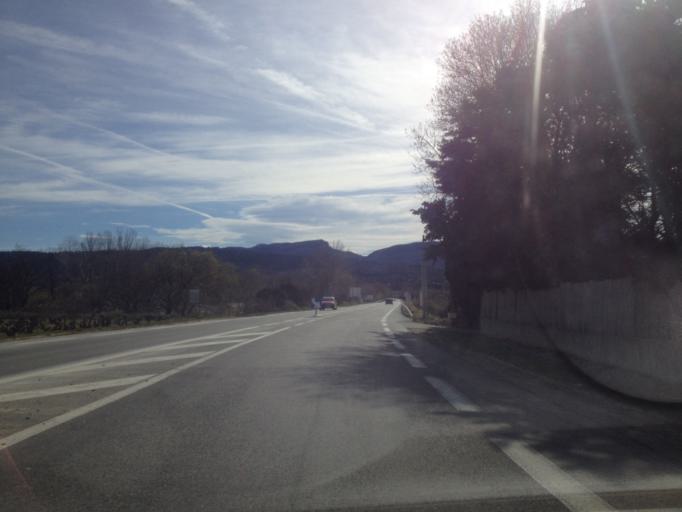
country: FR
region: Provence-Alpes-Cote d'Azur
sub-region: Departement du Vaucluse
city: Sablet
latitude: 44.1956
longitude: 4.9799
